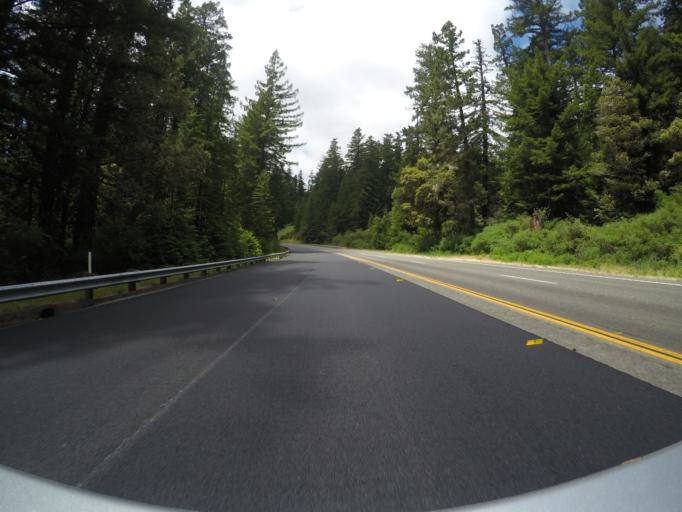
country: US
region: California
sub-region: Humboldt County
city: Redway
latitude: 40.3036
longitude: -123.8937
